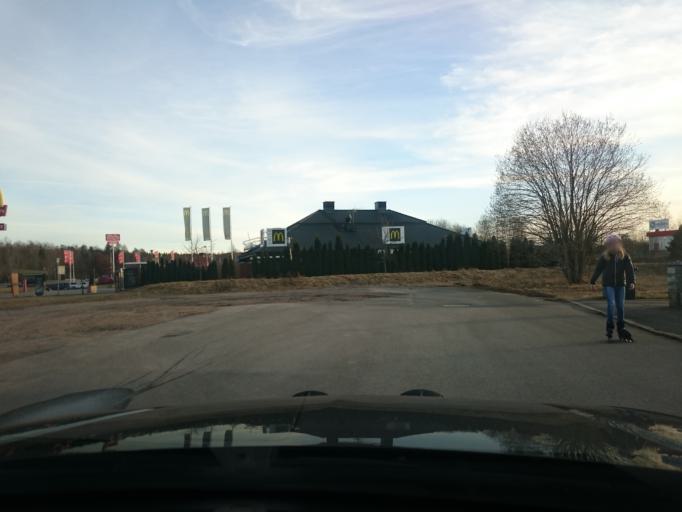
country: SE
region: Joenkoeping
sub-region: Vetlanda Kommun
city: Vetlanda
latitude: 57.4163
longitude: 15.0909
